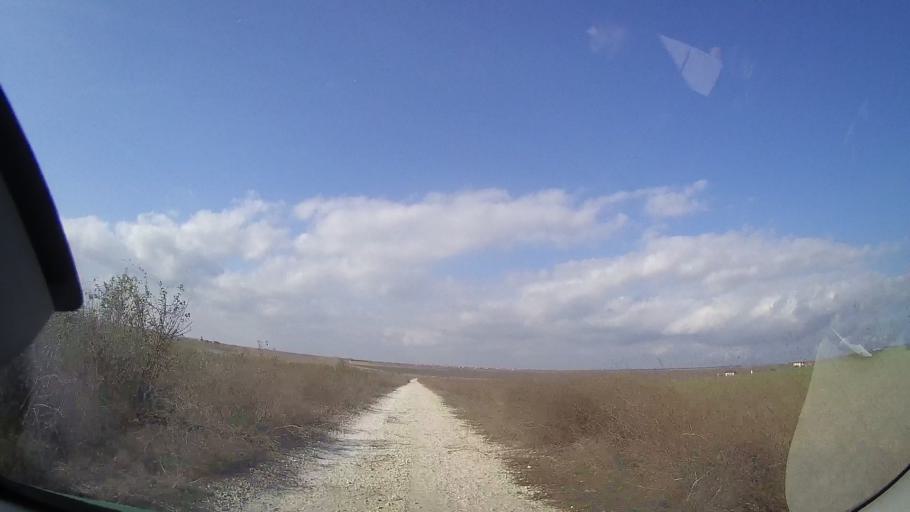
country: RO
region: Constanta
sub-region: Comuna Douazeci si Trei August
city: Douazeci si Trei August
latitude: 43.9054
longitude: 28.6155
